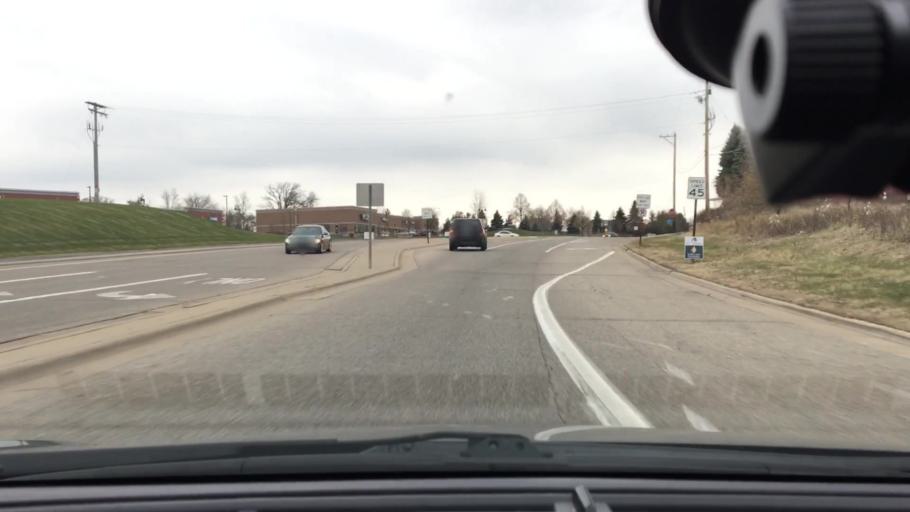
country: US
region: Minnesota
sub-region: Hennepin County
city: Corcoran
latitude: 45.0443
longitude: -93.5258
